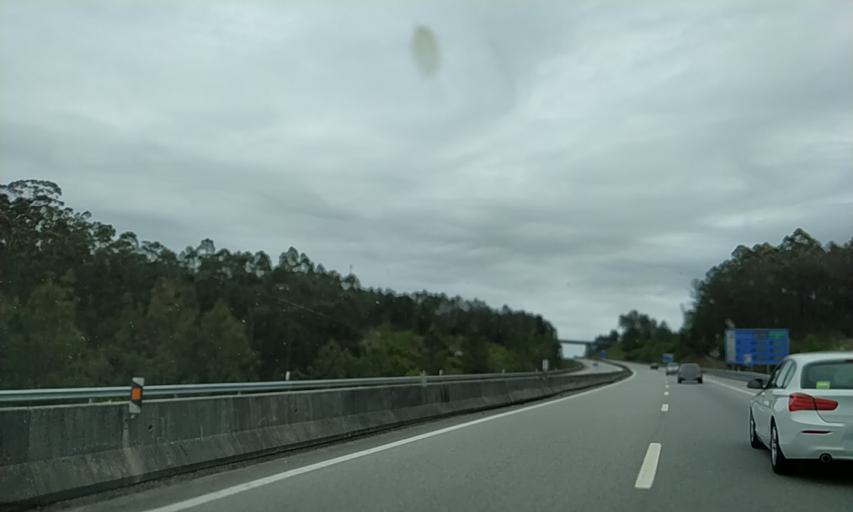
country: PT
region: Viseu
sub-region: Viseu
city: Viseu
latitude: 40.6242
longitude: -7.9521
